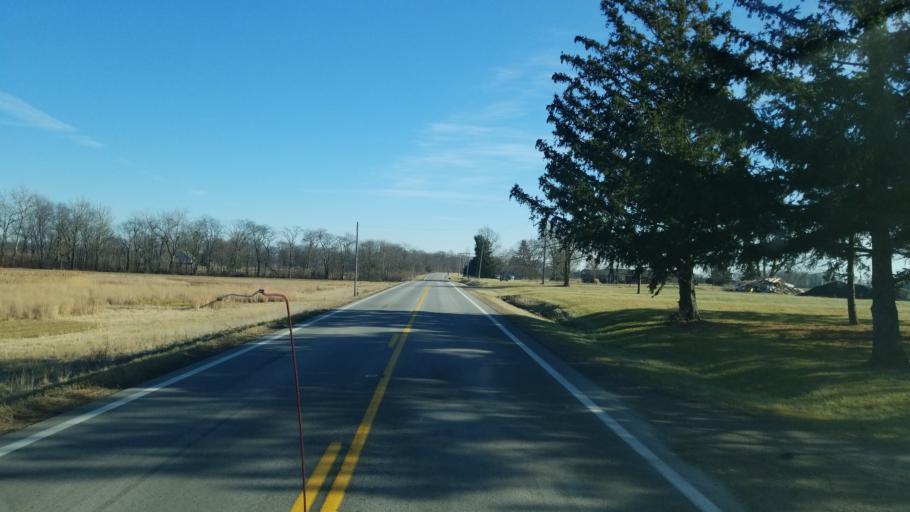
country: US
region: Ohio
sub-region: Henry County
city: Liberty Center
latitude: 41.4145
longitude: -83.9057
